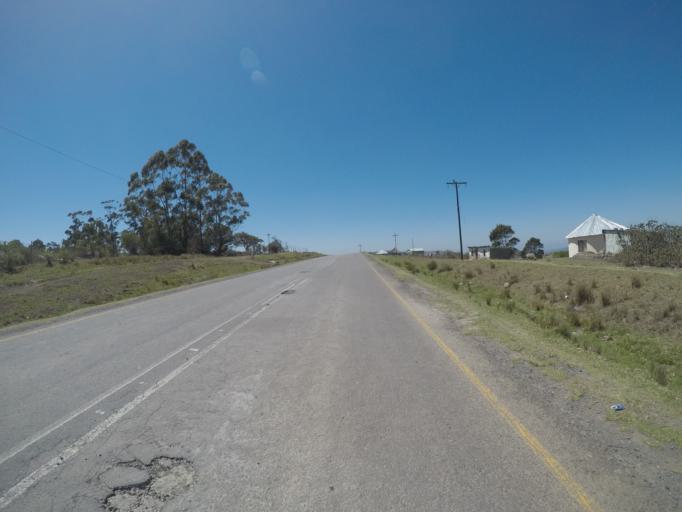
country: ZA
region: Eastern Cape
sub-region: OR Tambo District Municipality
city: Mthatha
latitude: -31.8979
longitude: 28.9370
